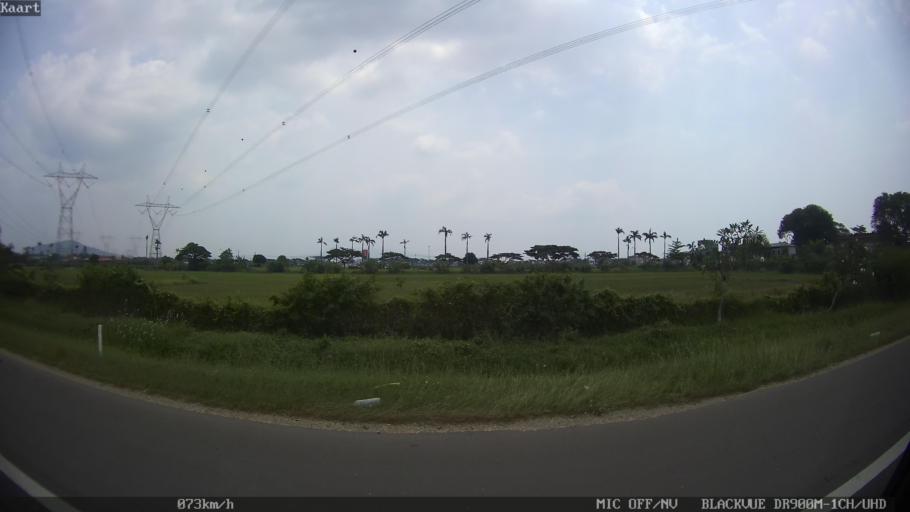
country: ID
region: Banten
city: Bojonegara
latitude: -6.0150
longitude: 106.0836
